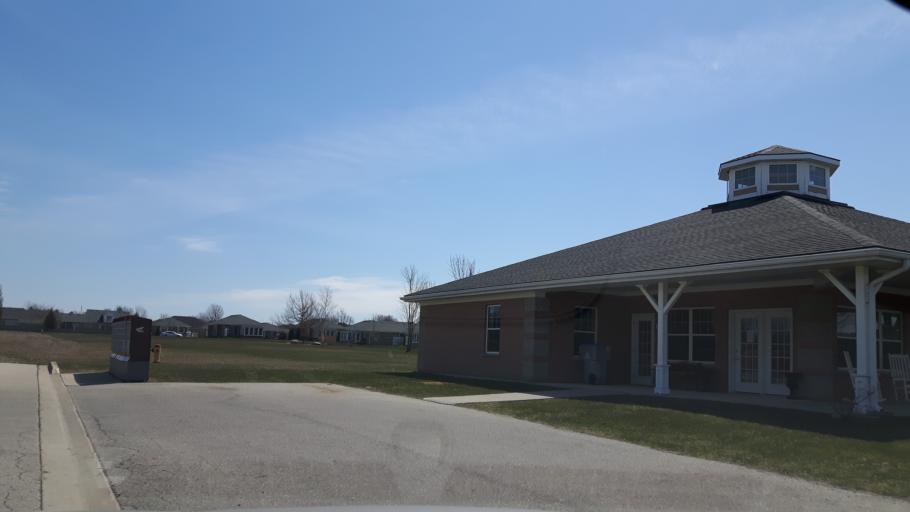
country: CA
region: Ontario
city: Goderich
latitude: 43.7293
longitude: -81.7233
